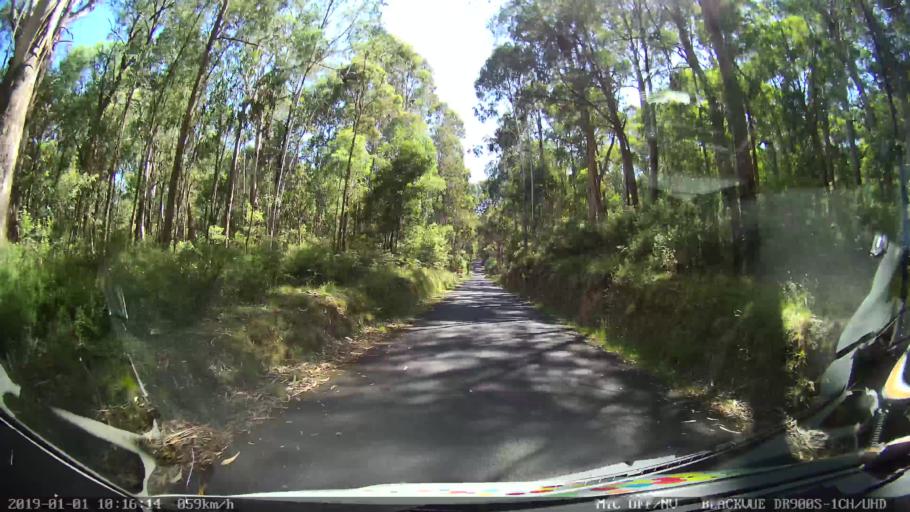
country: AU
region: New South Wales
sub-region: Snowy River
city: Jindabyne
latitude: -36.0952
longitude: 148.1656
